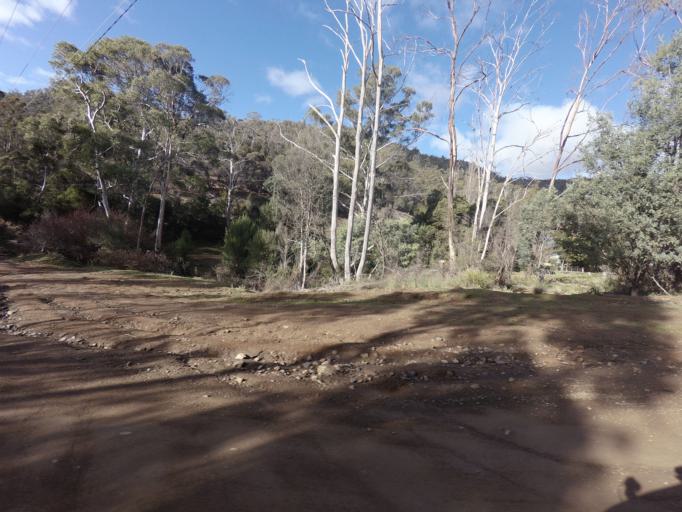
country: AU
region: Tasmania
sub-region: Derwent Valley
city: New Norfolk
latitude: -42.8167
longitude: 147.1280
